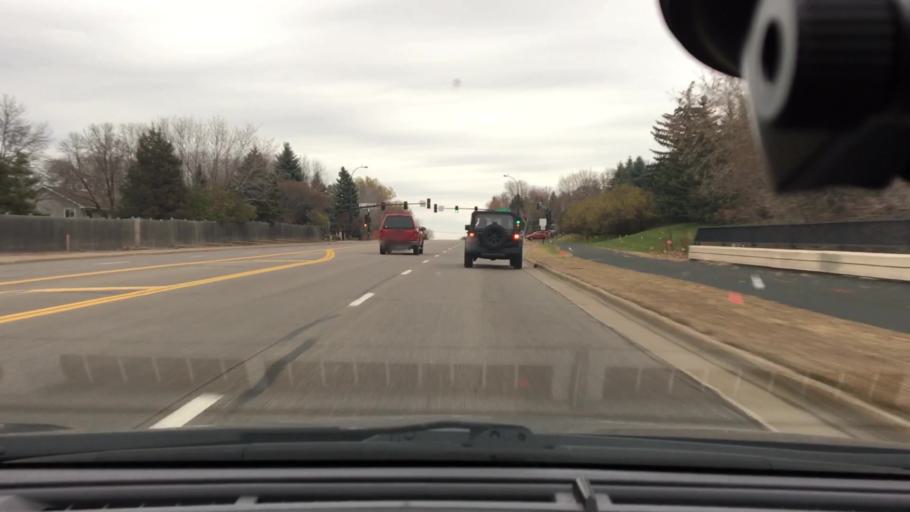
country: US
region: Minnesota
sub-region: Hennepin County
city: Maple Grove
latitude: 45.1235
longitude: -93.4588
